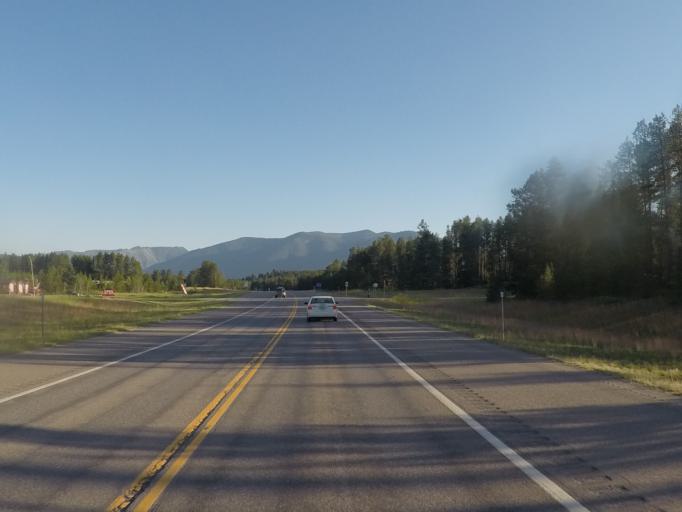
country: US
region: Montana
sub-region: Flathead County
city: Columbia Falls
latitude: 48.4387
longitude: -114.0413
